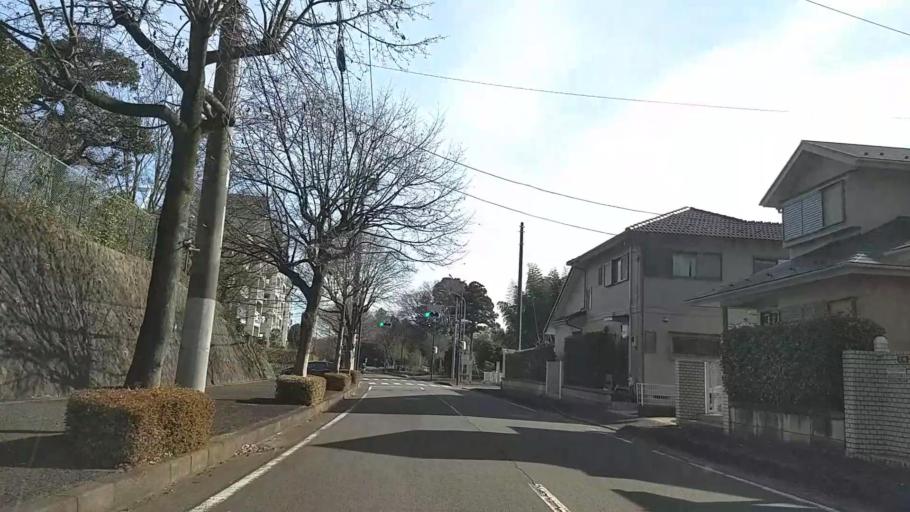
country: JP
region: Kanagawa
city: Hadano
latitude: 35.3534
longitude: 139.2247
